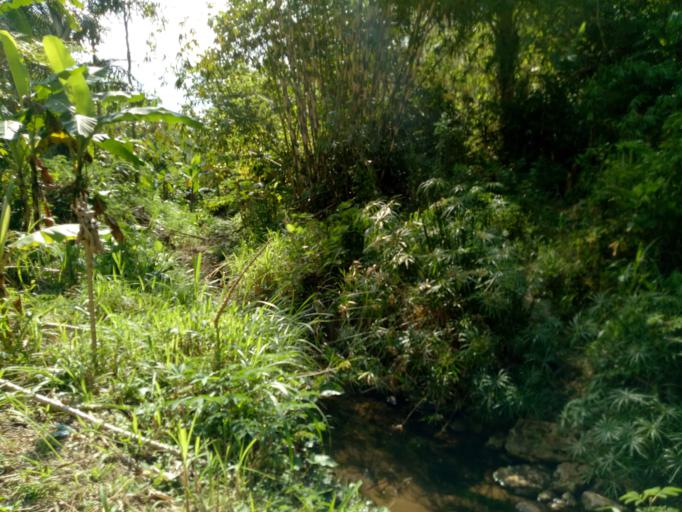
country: ID
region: East Java
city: Pagak
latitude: -8.2067
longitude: 112.5314
